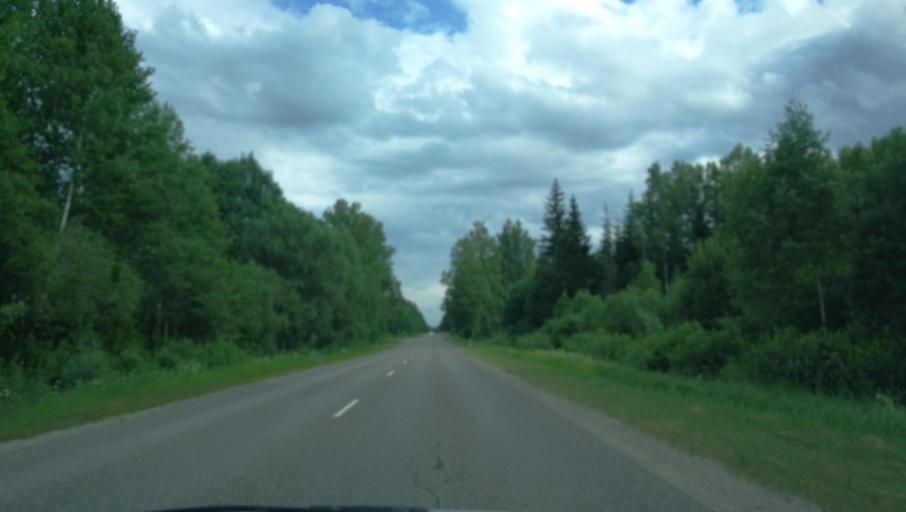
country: LV
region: Naukseni
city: Naukseni
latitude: 57.8163
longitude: 25.4021
